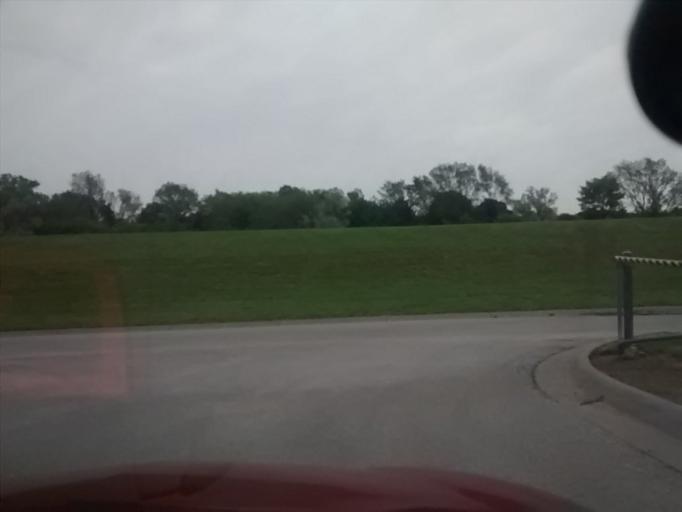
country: US
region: Nebraska
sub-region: Sarpy County
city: Offutt Air Force Base
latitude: 41.1651
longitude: -95.9340
